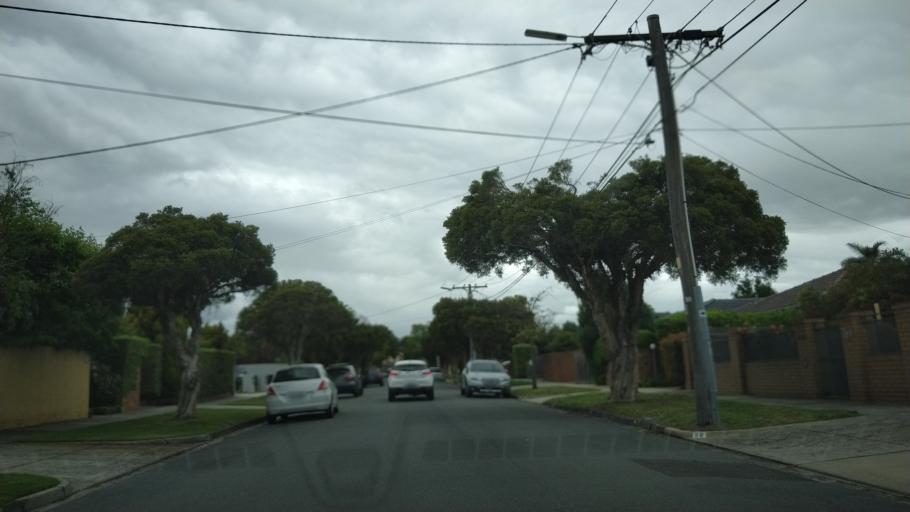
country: AU
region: Victoria
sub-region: Glen Eira
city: Caulfield
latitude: -37.8841
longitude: 145.0273
